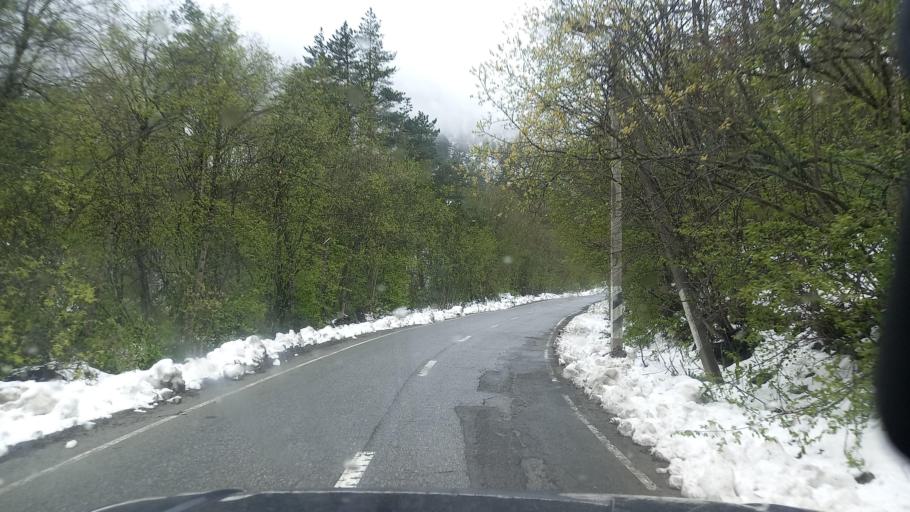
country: RU
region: North Ossetia
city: Mizur
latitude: 42.7947
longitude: 43.9248
